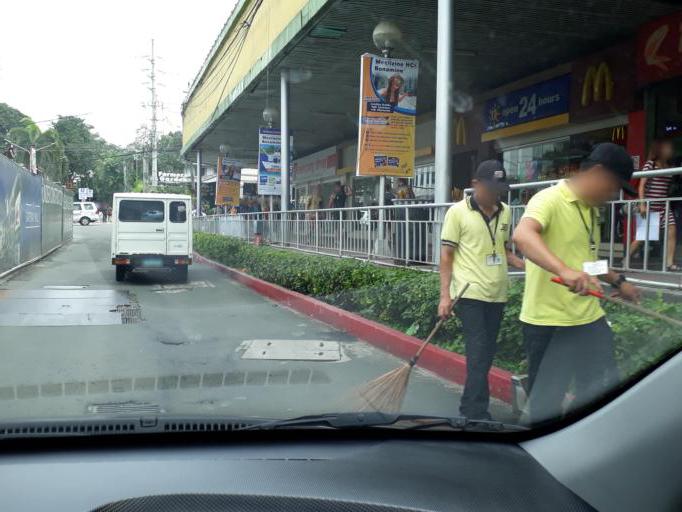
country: PH
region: Metro Manila
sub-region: San Juan
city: San Juan
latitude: 14.6197
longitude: 121.0530
